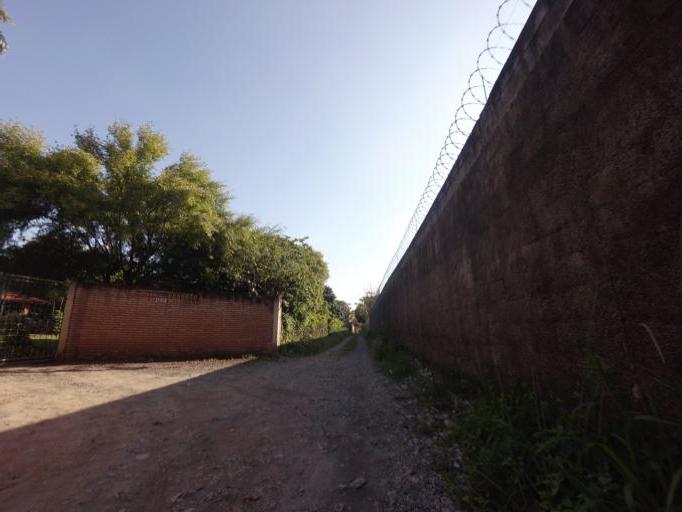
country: BR
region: Sao Paulo
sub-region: Piracicaba
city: Piracicaba
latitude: -22.7342
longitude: -47.5976
